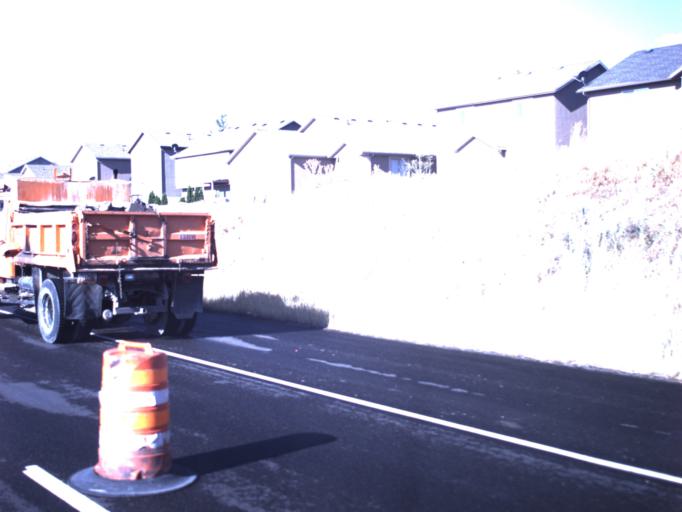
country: US
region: Utah
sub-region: Salt Lake County
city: Oquirrh
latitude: 40.6070
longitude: -112.0561
